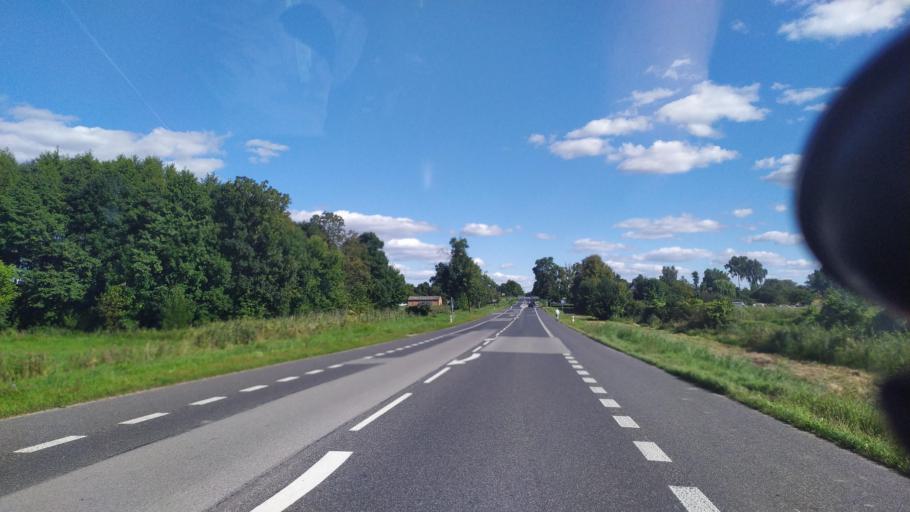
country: PL
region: Lublin Voivodeship
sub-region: Powiat lubelski
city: Garbow
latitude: 51.3614
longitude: 22.3091
